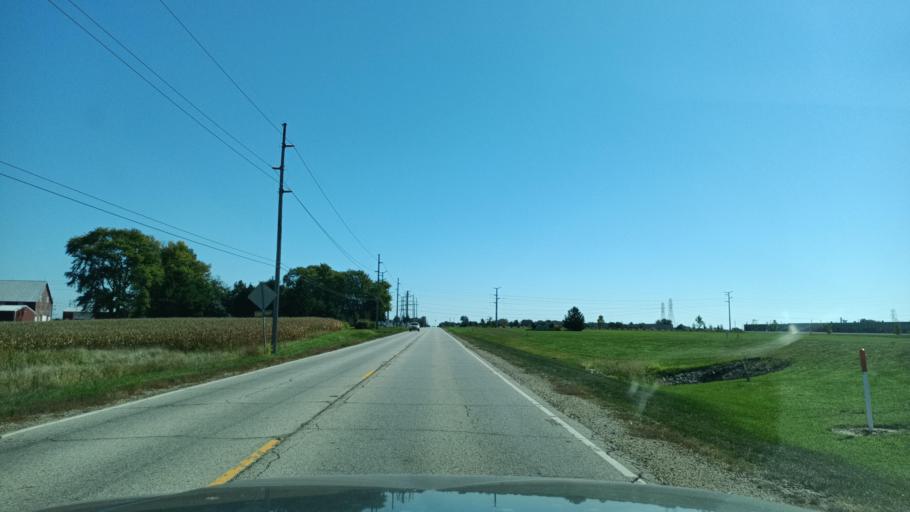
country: US
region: Illinois
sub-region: Peoria County
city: Dunlap
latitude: 40.7831
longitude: -89.7063
